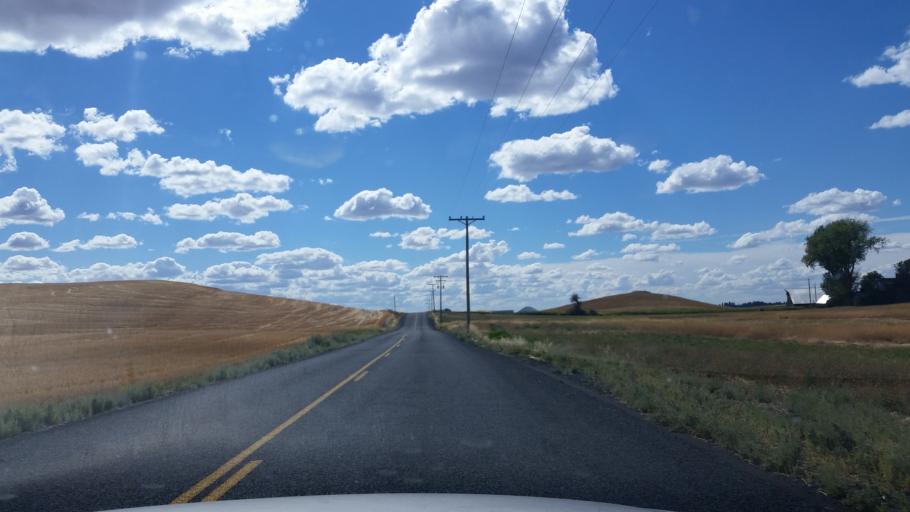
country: US
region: Washington
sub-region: Spokane County
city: Cheney
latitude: 47.3828
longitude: -117.4915
